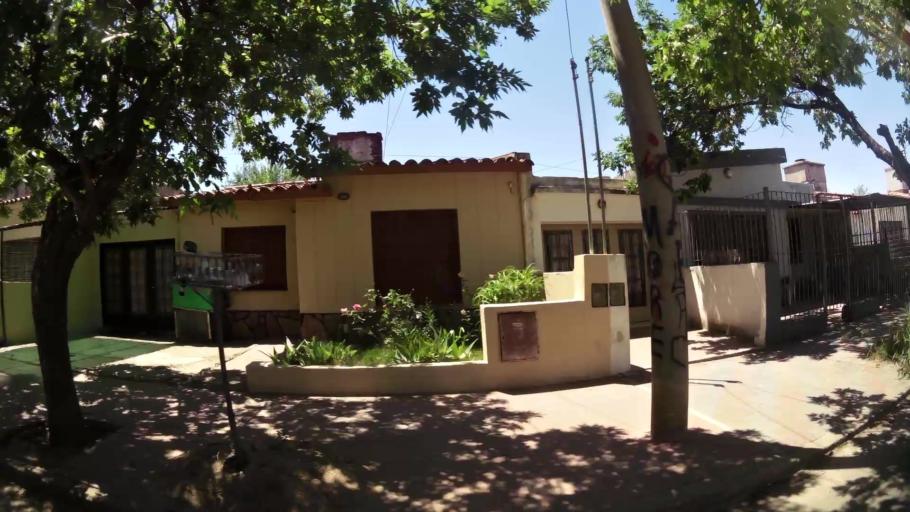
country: AR
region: Cordoba
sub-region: Departamento de Capital
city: Cordoba
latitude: -31.4326
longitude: -64.1272
